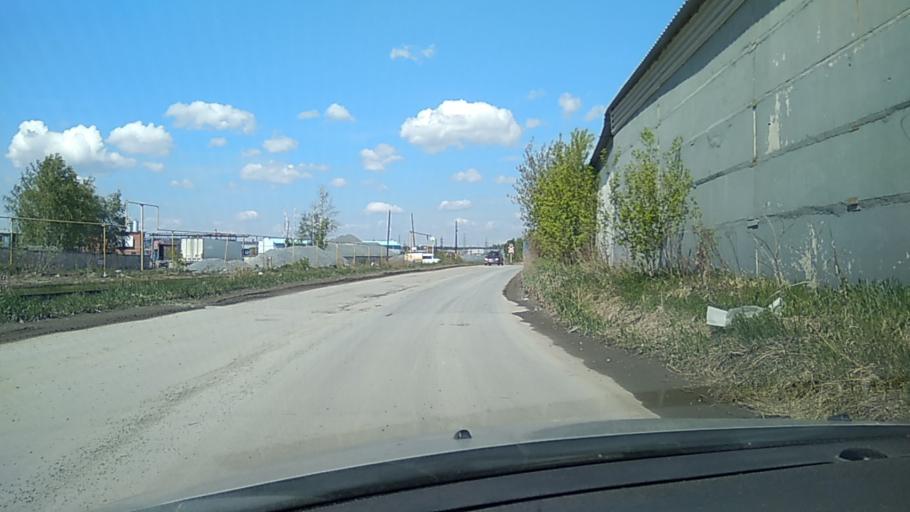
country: RU
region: Sverdlovsk
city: Istok
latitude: 56.7538
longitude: 60.7531
